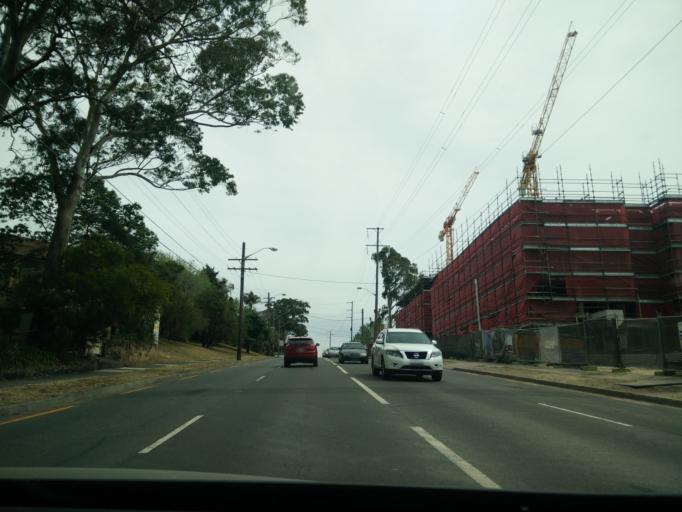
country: AU
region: New South Wales
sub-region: Parramatta
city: Epping
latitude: -33.7718
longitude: 151.0774
